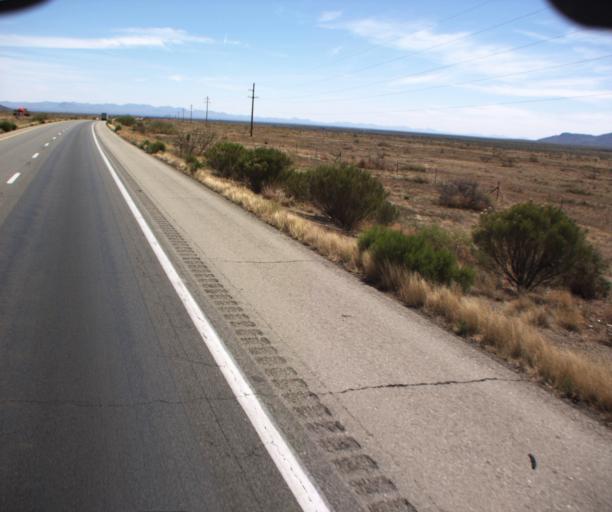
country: US
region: Arizona
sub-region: Cochise County
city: Willcox
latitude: 32.3621
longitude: -109.6509
